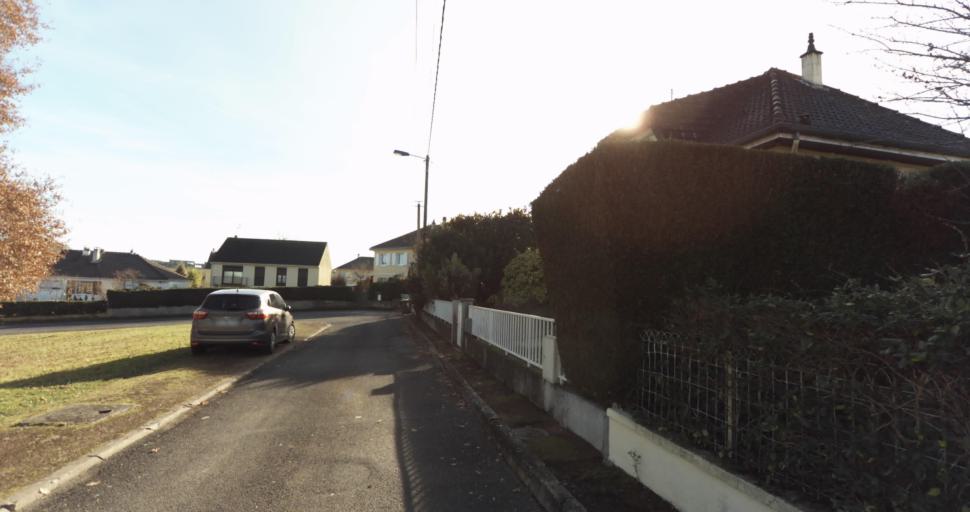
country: FR
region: Limousin
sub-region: Departement de la Haute-Vienne
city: Aixe-sur-Vienne
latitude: 45.7926
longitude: 1.1258
